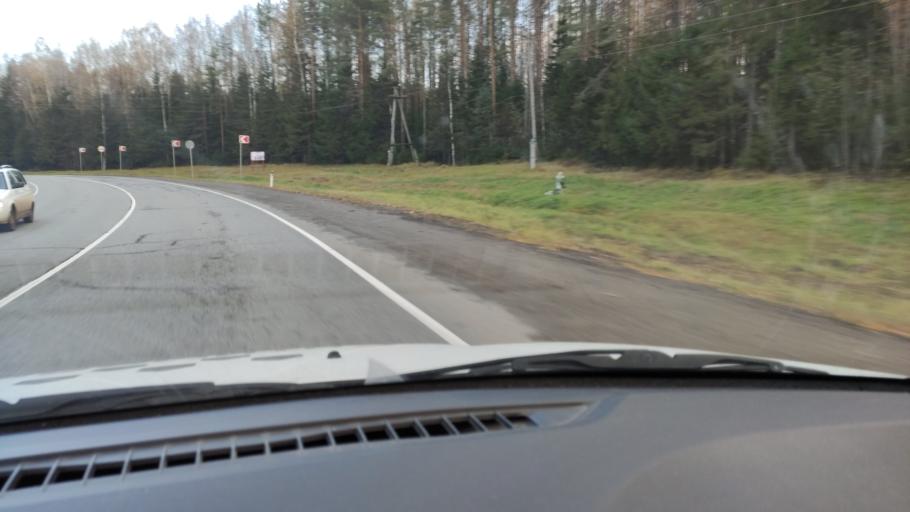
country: RU
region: Kirov
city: Belaya Kholunitsa
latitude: 58.9039
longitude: 50.9498
